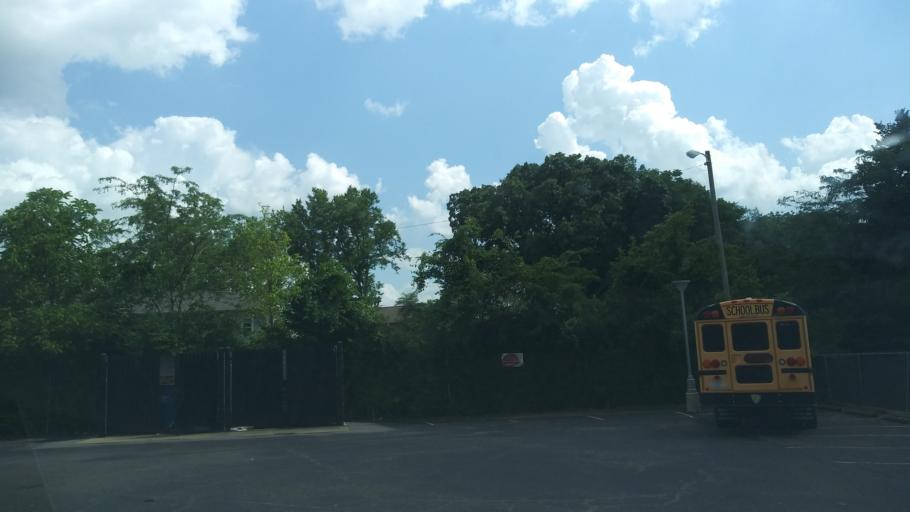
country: US
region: Tennessee
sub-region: Davidson County
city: Nashville
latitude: 36.1447
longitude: -86.8276
